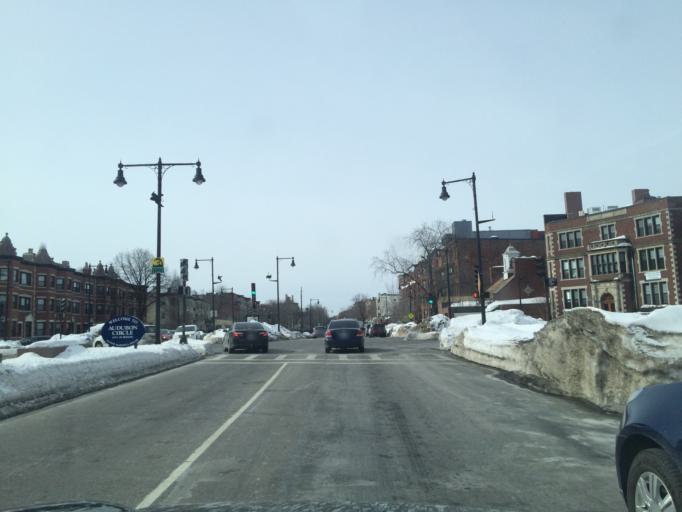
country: US
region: Massachusetts
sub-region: Norfolk County
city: Brookline
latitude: 42.3468
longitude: -71.1046
